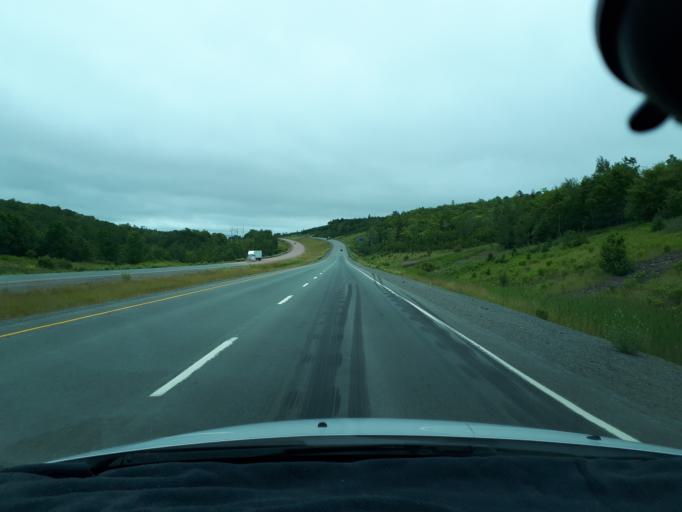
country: CA
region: Nova Scotia
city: Pictou
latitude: 45.5437
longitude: -62.8333
